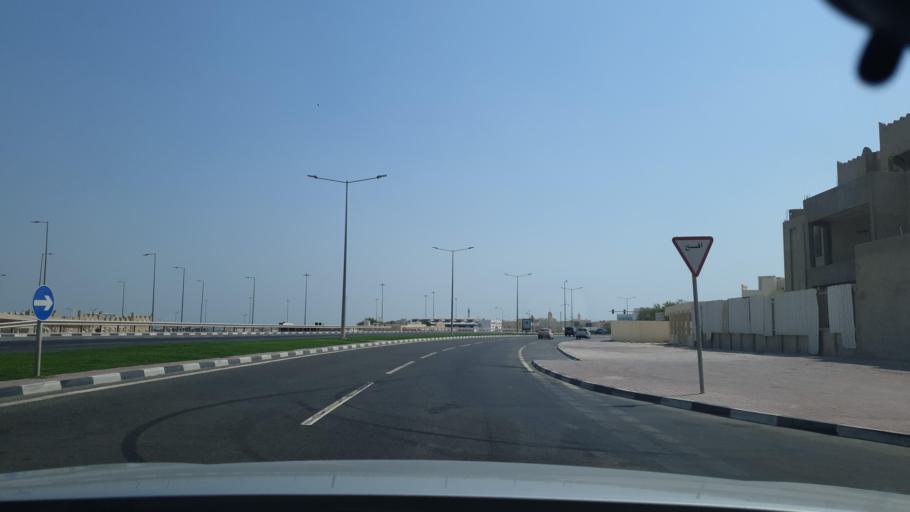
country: QA
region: Al Khawr
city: Al Khawr
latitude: 25.6862
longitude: 51.5133
